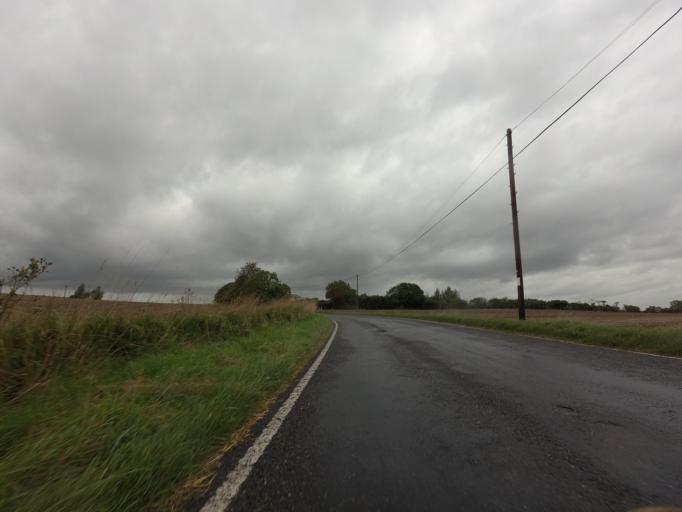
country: GB
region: England
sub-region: Cambridgeshire
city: Comberton
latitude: 52.1707
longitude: -0.0145
